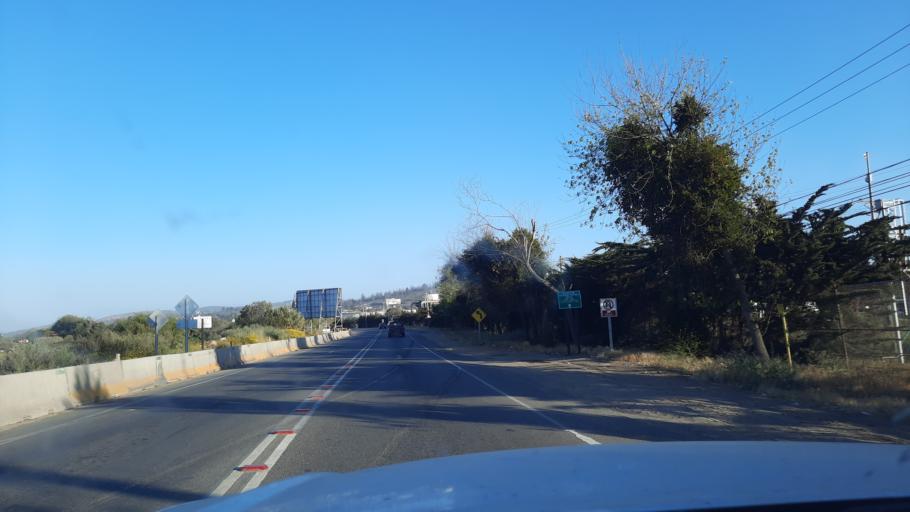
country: CL
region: Valparaiso
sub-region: Provincia de Valparaiso
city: Vina del Mar
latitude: -32.9223
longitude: -71.5042
